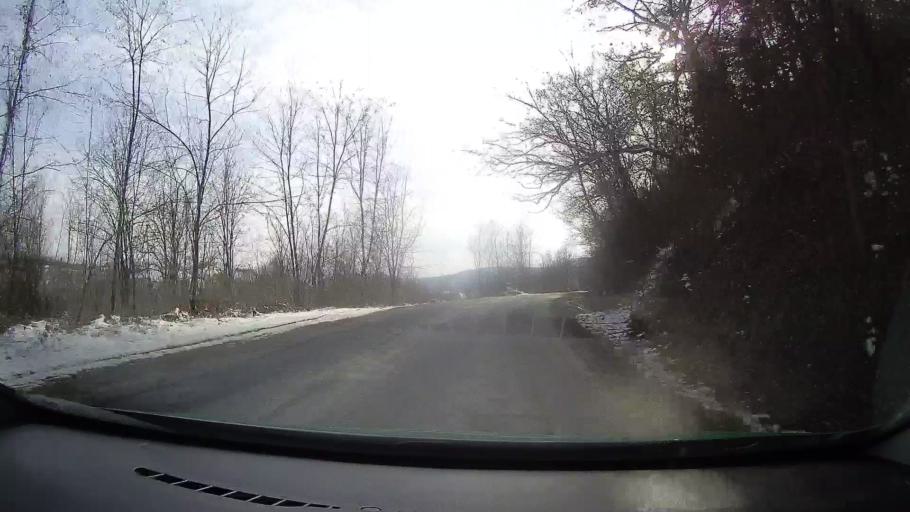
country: RO
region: Mures
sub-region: Comuna Apold
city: Saes
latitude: 46.1877
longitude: 24.7635
